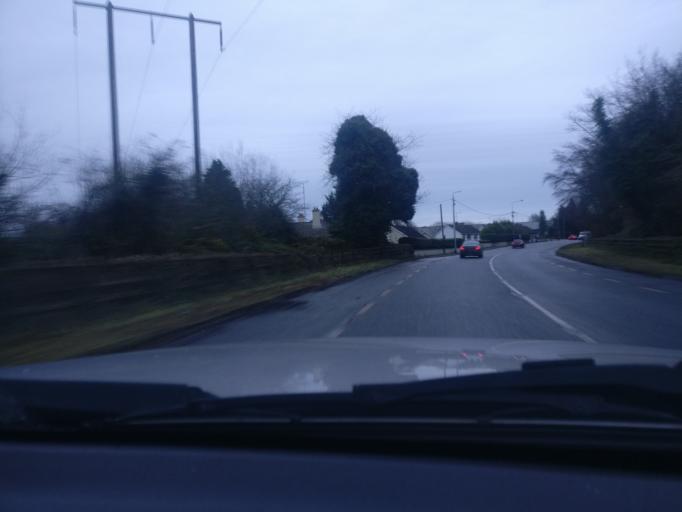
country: IE
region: Leinster
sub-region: An Mhi
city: Navan
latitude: 53.6564
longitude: -6.7061
